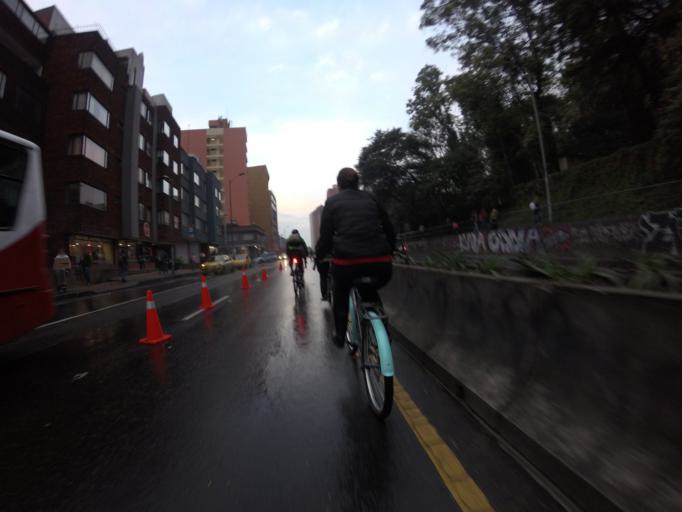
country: CO
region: Bogota D.C.
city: Bogota
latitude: 4.6298
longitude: -74.0648
